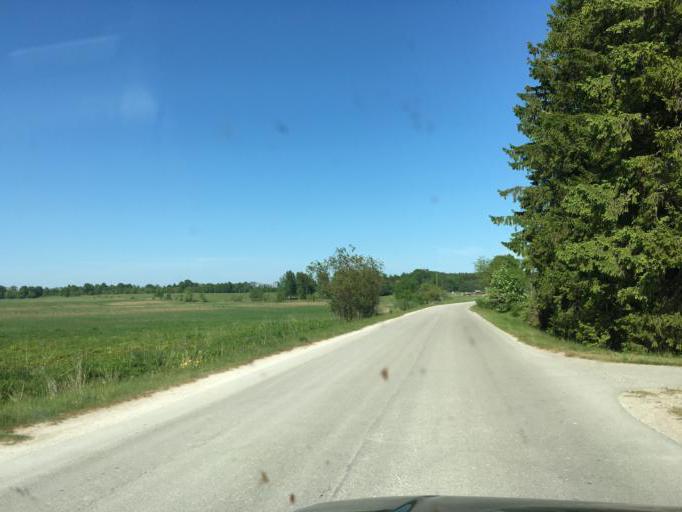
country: LV
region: Dundaga
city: Dundaga
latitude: 57.6078
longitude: 22.4543
